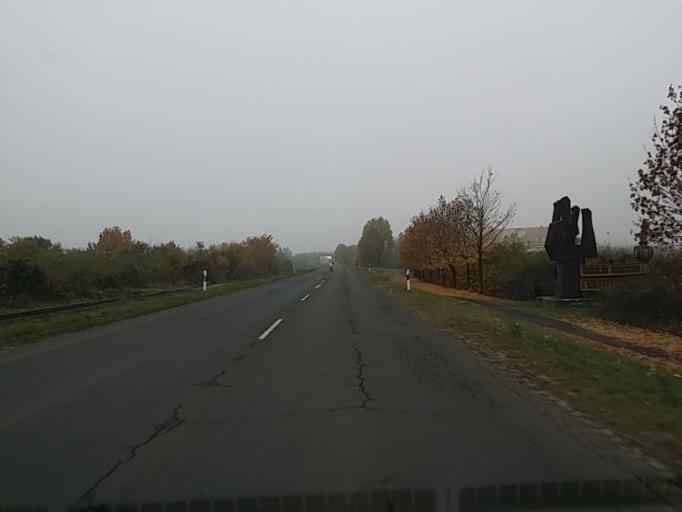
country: HU
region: Heves
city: Gyongyossolymos
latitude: 47.8002
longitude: 19.9467
